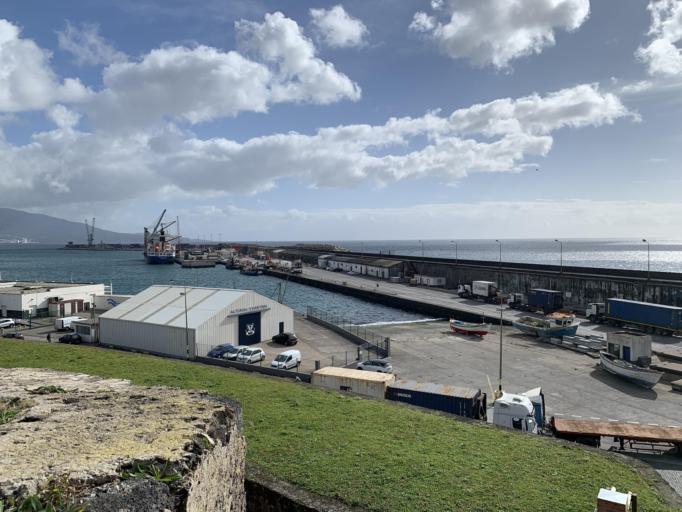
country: PT
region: Azores
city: Ponta Delgada
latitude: 37.7360
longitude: -25.6727
